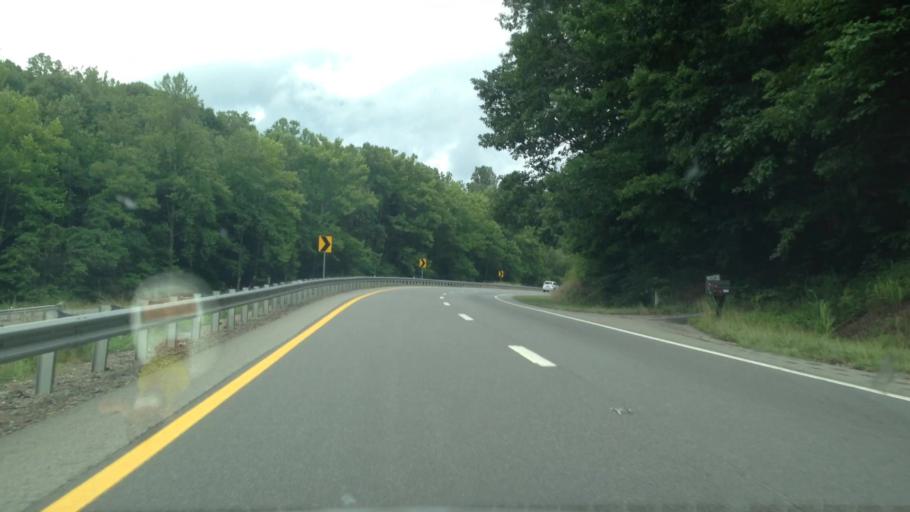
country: US
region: Virginia
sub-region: Henry County
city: Stanleytown
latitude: 36.7813
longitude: -79.9367
